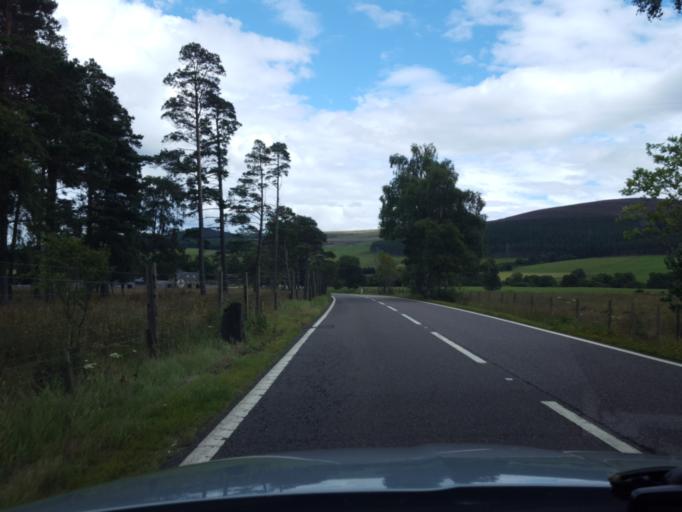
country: GB
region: Scotland
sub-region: Highland
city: Grantown on Spey
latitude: 57.3899
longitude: -3.4428
